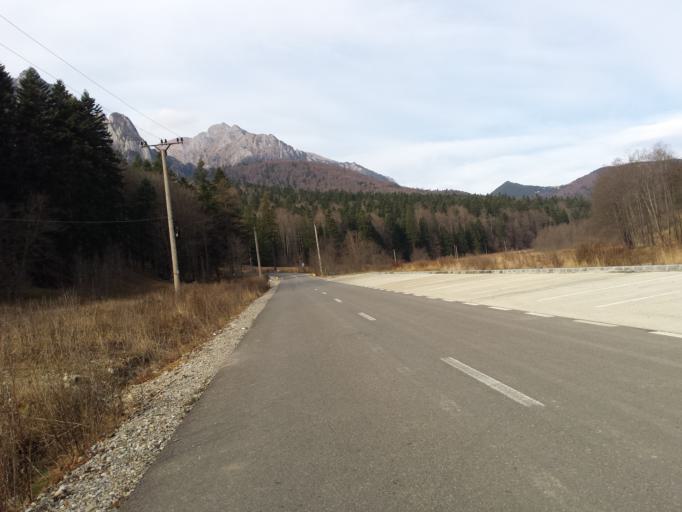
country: RO
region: Prahova
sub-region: Oras Azuga
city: Azuga
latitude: 45.4293
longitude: 25.5352
